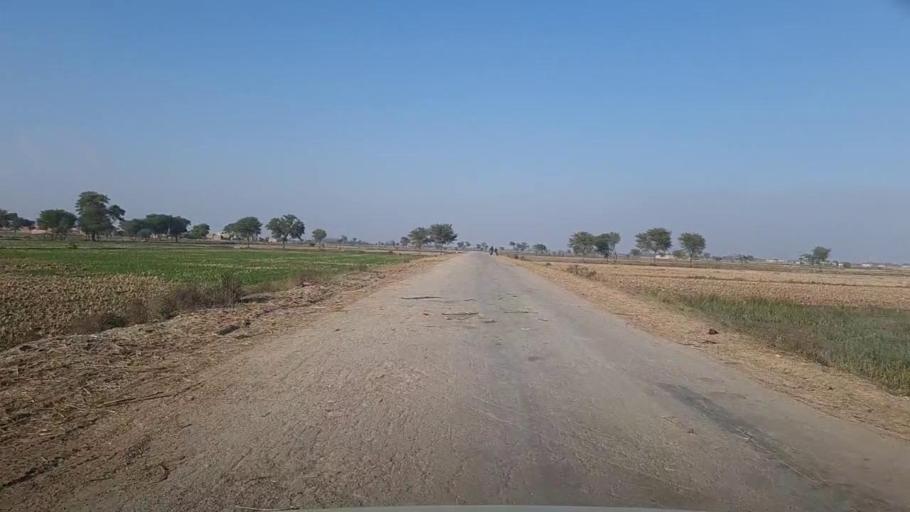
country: PK
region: Sindh
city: Phulji
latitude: 26.8630
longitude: 67.7946
